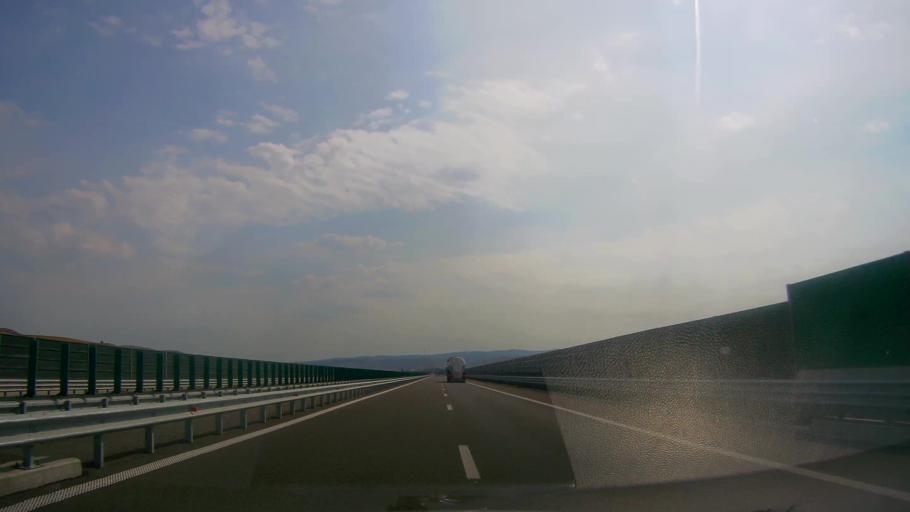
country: RO
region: Cluj
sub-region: Comuna Floresti
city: Luna de Sus
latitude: 46.7606
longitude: 23.3973
